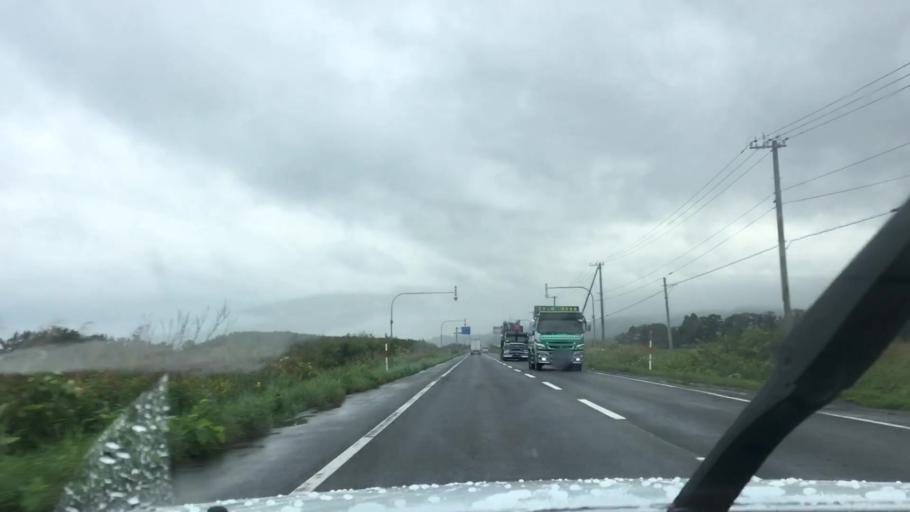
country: JP
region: Hokkaido
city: Niseko Town
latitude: 42.3941
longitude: 140.3000
